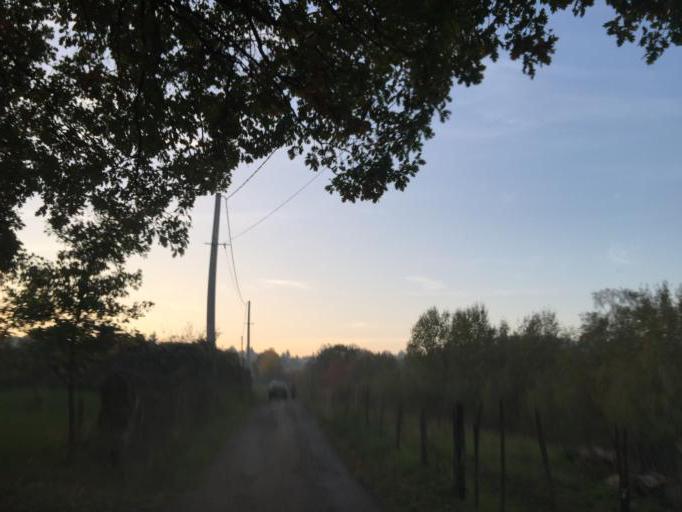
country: FR
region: Rhone-Alpes
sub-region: Departement de la Loire
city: Saint-Chamond
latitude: 45.4887
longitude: 4.5034
